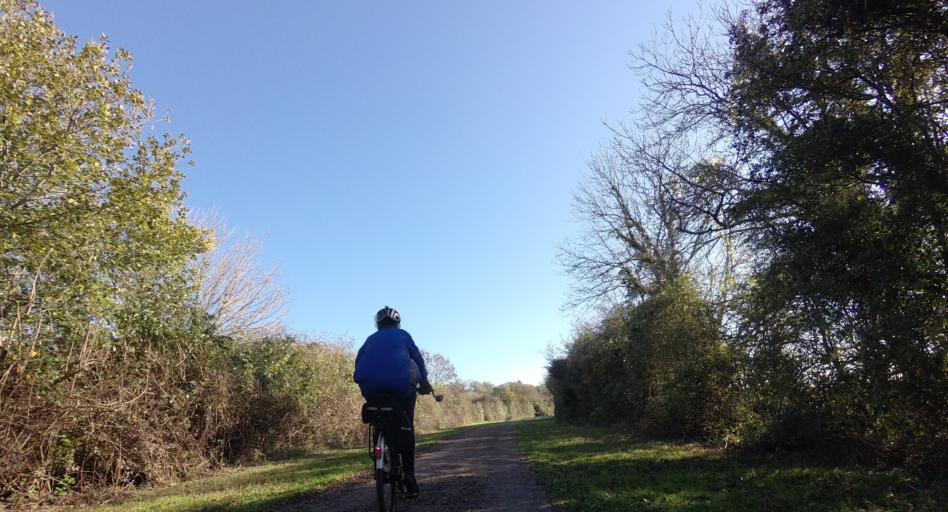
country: GB
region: England
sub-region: West Sussex
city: Shoreham-by-Sea
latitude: 50.8599
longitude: -0.2936
